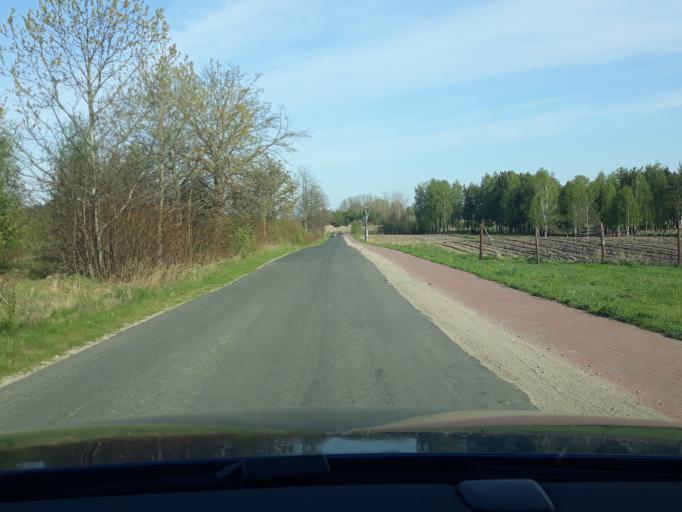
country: PL
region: Pomeranian Voivodeship
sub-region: Powiat czluchowski
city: Przechlewo
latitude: 53.8327
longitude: 17.3706
